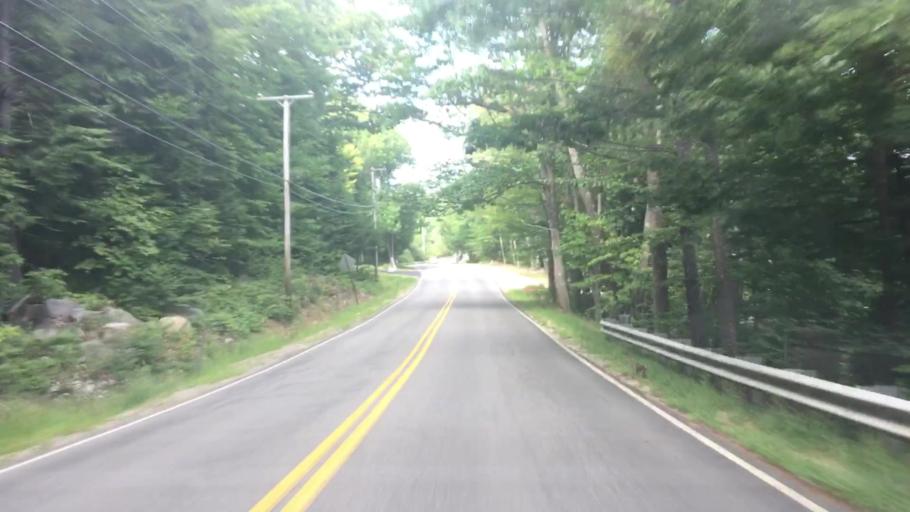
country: US
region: Maine
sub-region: Oxford County
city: Oxford
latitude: 44.1082
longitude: -70.5079
